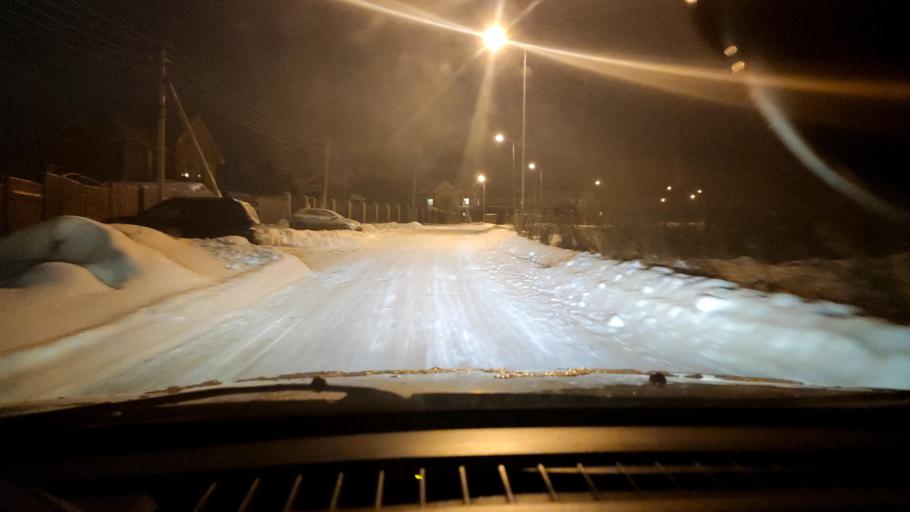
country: RU
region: Perm
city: Perm
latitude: 58.0273
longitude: 56.3449
